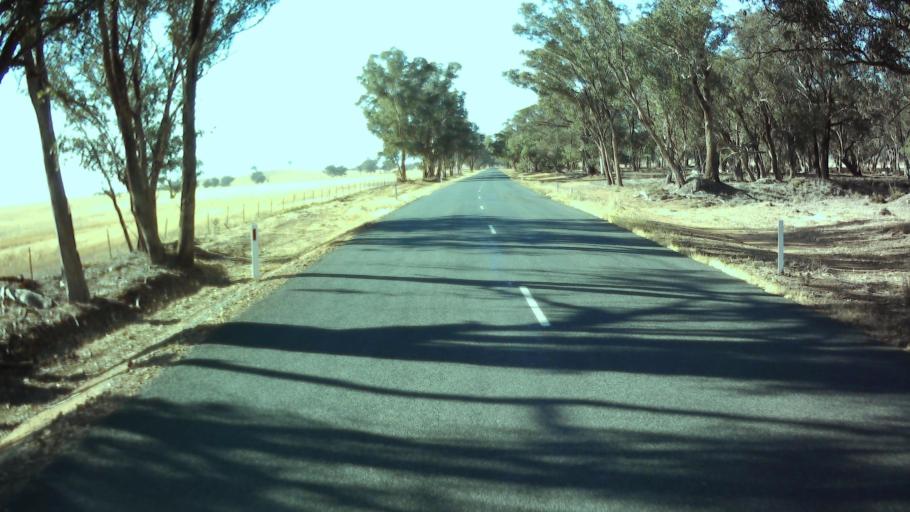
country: AU
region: New South Wales
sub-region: Weddin
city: Grenfell
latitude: -33.9516
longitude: 148.1386
